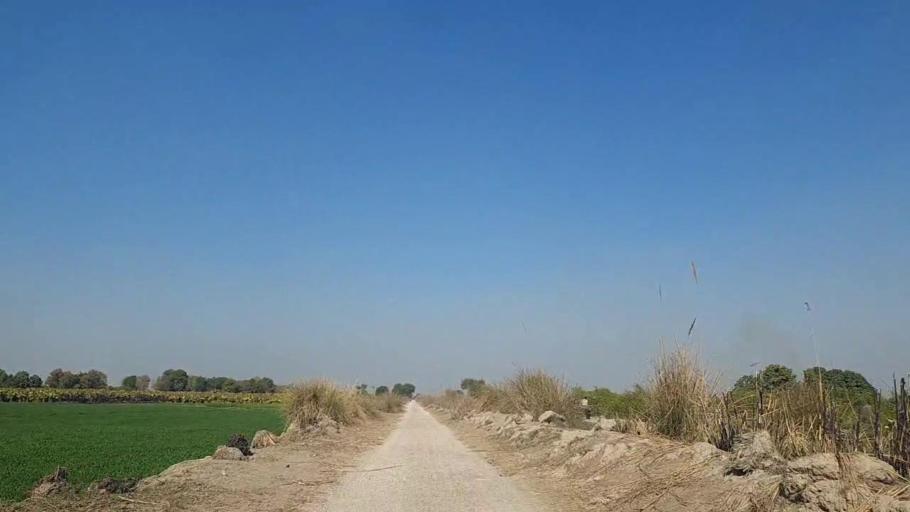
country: PK
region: Sindh
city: Sakrand
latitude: 26.2579
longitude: 68.2208
